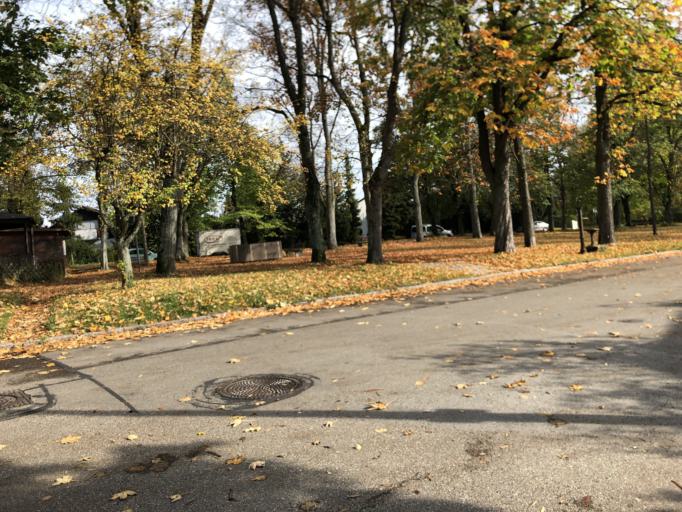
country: DE
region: Baden-Wuerttemberg
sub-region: Regierungsbezirk Stuttgart
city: Sindelfingen
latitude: 48.7170
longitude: 8.9976
